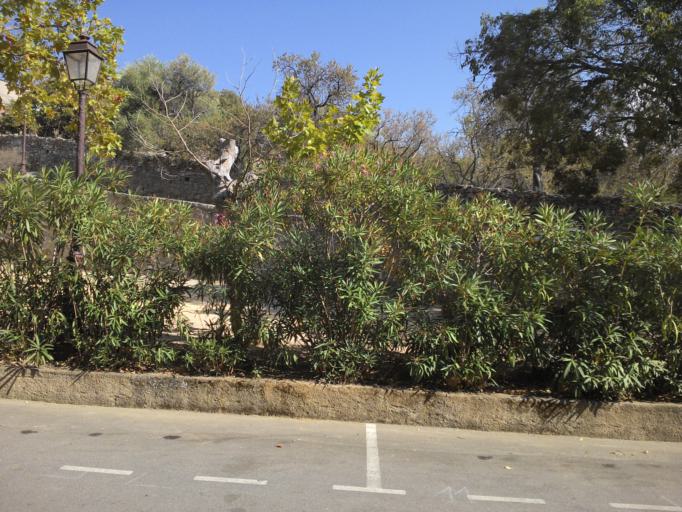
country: FR
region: Corsica
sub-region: Departement de la Haute-Corse
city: Lumio
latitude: 42.5820
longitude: 8.8951
